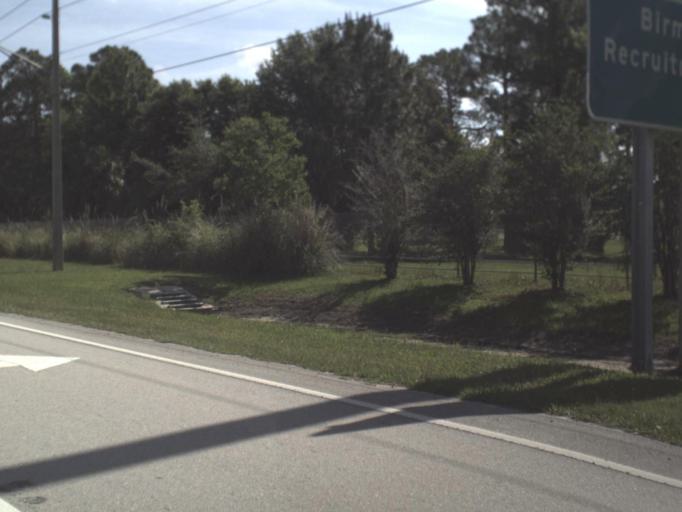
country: US
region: Florida
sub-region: Clay County
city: Orange Park
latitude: 30.2196
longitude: -81.7023
